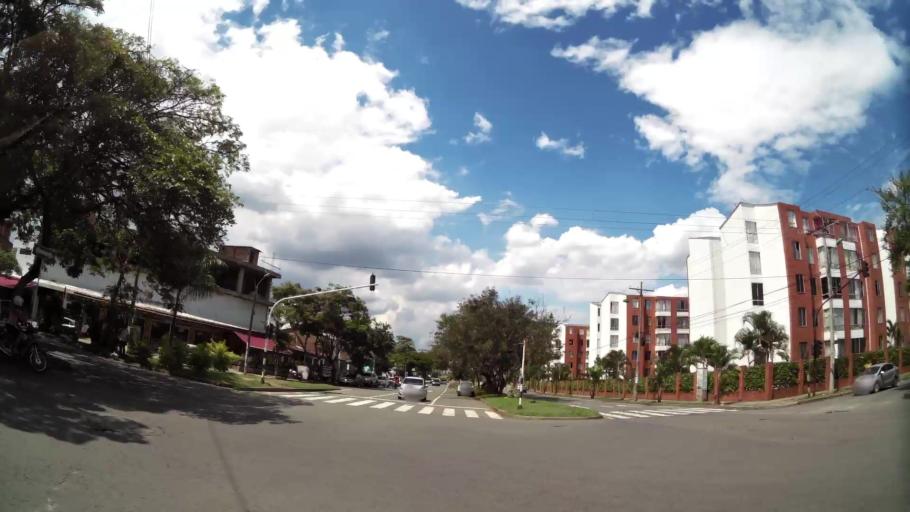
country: CO
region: Valle del Cauca
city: Cali
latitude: 3.3837
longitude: -76.5204
